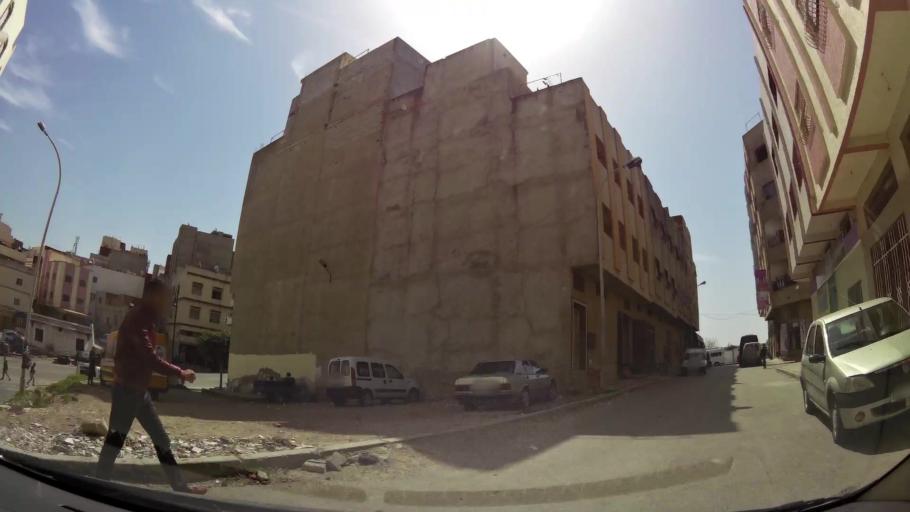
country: MA
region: Tanger-Tetouan
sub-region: Tanger-Assilah
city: Tangier
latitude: 35.7405
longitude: -5.8063
